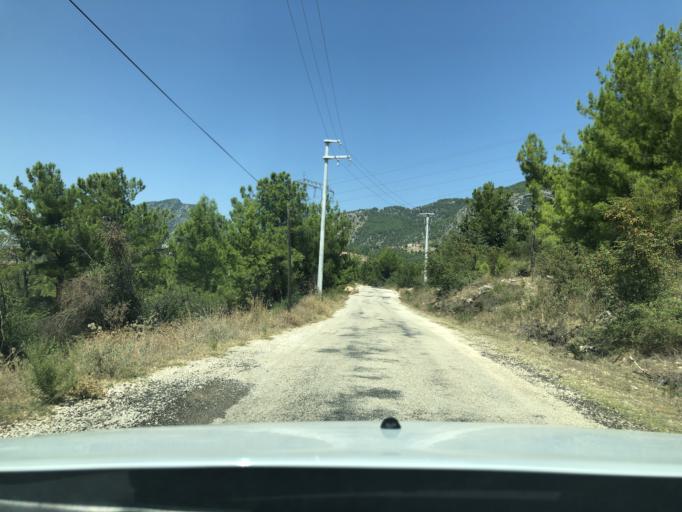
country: TR
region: Antalya
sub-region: Manavgat
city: Manavgat
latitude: 36.8741
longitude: 31.5500
